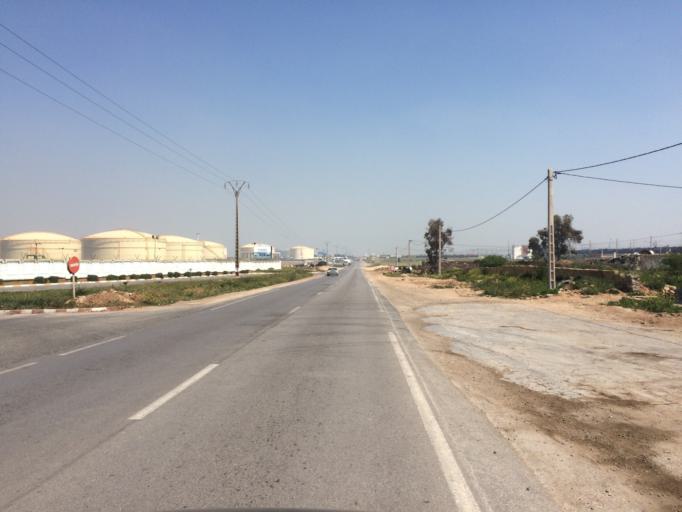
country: MA
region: Doukkala-Abda
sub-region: El-Jadida
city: Moulay Abdallah
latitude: 33.1417
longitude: -8.6084
